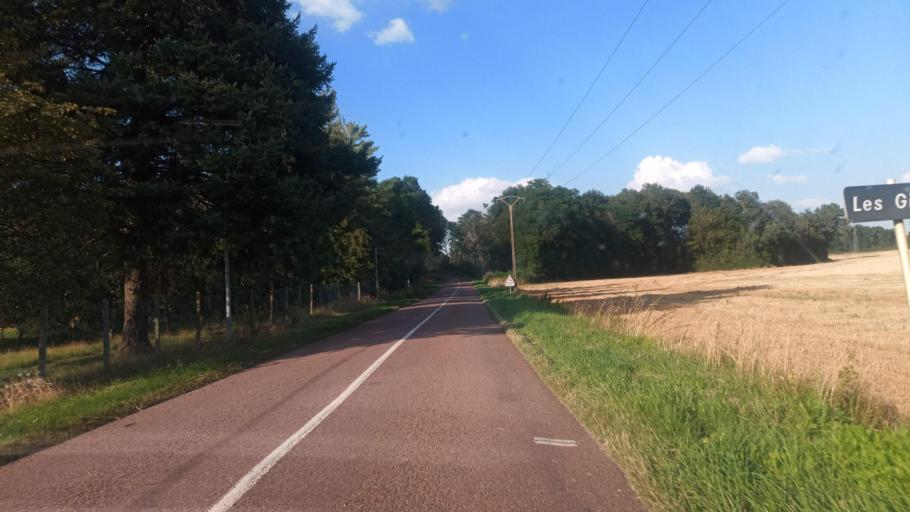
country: FR
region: Bourgogne
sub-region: Departement de l'Yonne
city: Pont-sur-Yonne
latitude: 48.2534
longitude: 3.1672
